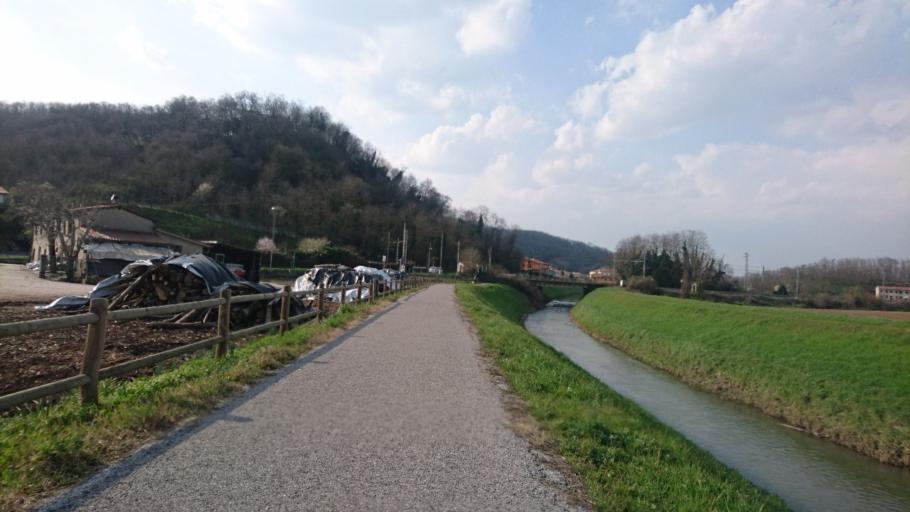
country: IT
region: Veneto
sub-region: Provincia di Padova
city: Montegrotto Terme
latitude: 45.3113
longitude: 11.7899
